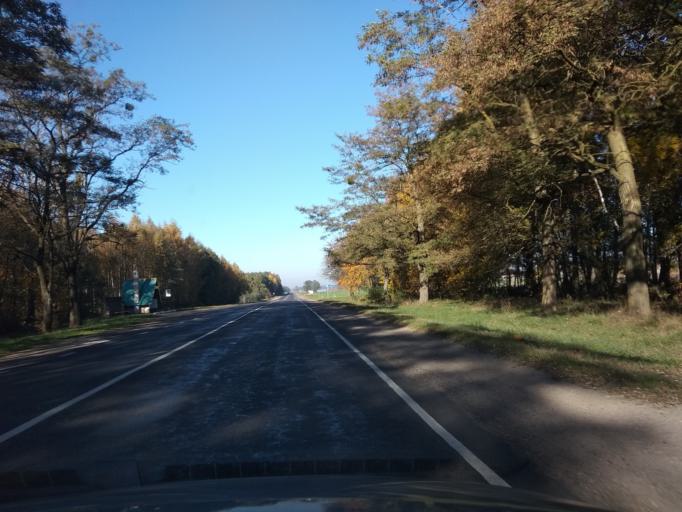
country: BY
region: Brest
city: Malaryta
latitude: 51.9330
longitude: 24.0546
